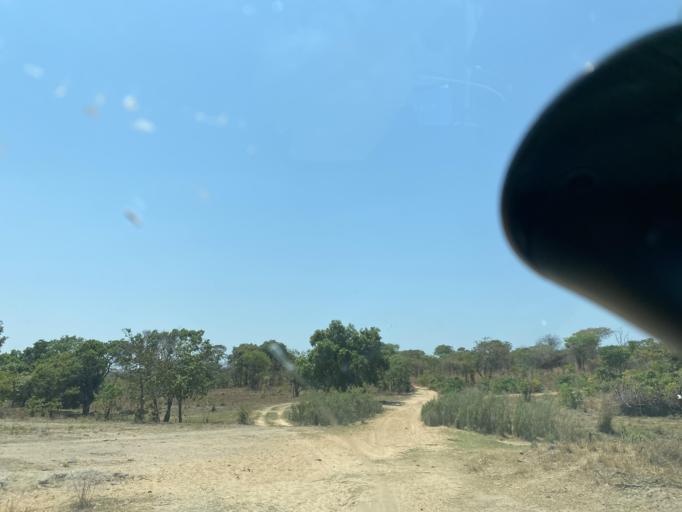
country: ZM
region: Lusaka
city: Chongwe
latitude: -15.4355
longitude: 29.1967
